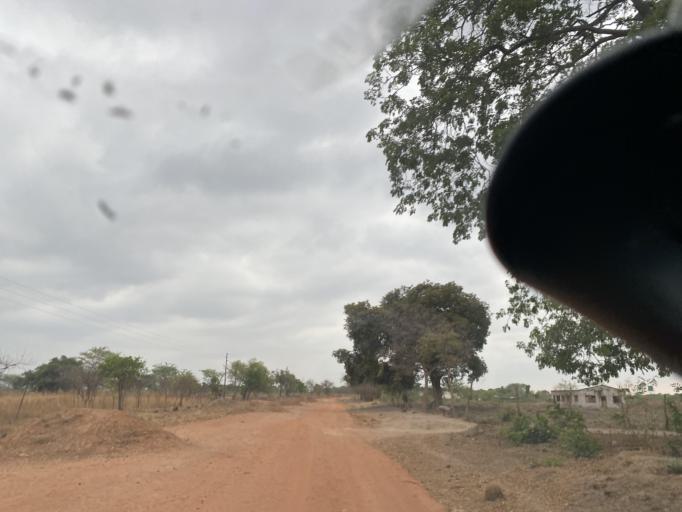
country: ZM
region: Lusaka
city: Chongwe
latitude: -15.2242
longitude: 28.7464
